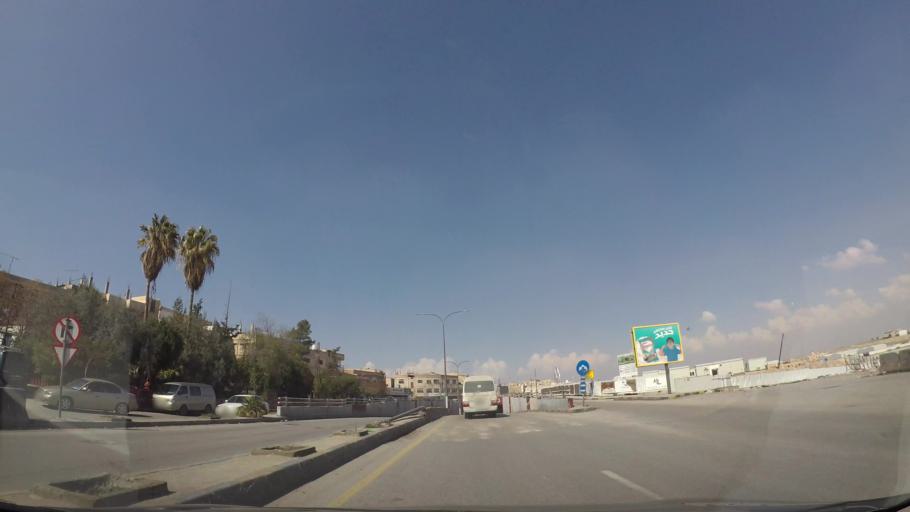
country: JO
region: Zarqa
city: Zarqa
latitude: 32.0709
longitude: 36.0981
